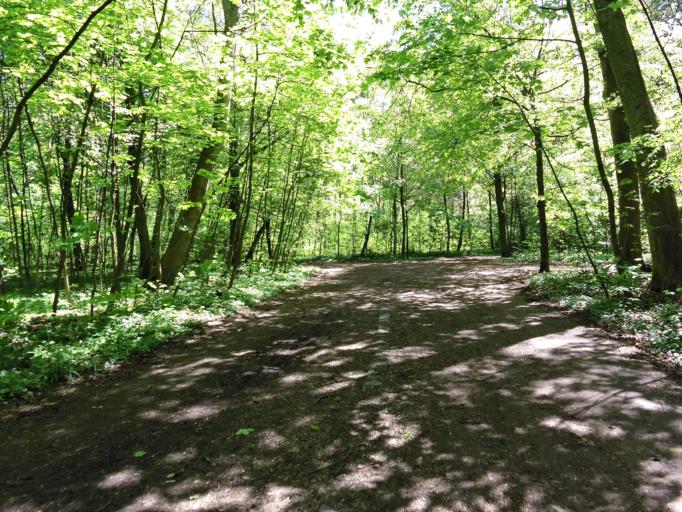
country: DE
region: Saxony
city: Leipzig
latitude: 51.3560
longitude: 12.3494
